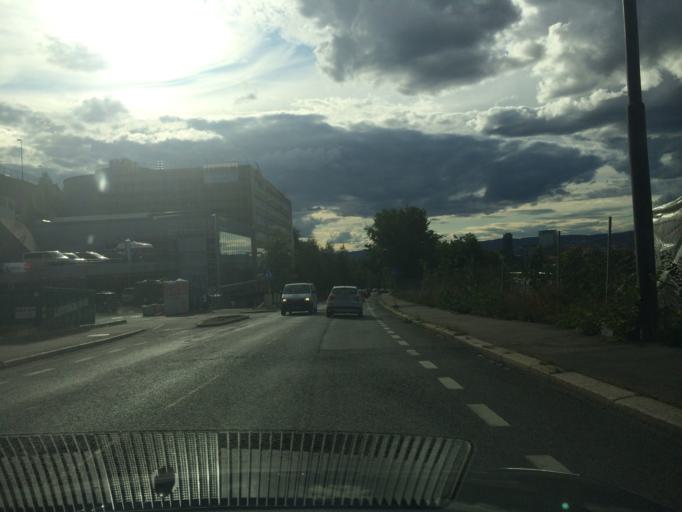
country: NO
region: Oslo
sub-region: Oslo
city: Oslo
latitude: 59.9020
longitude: 10.7862
